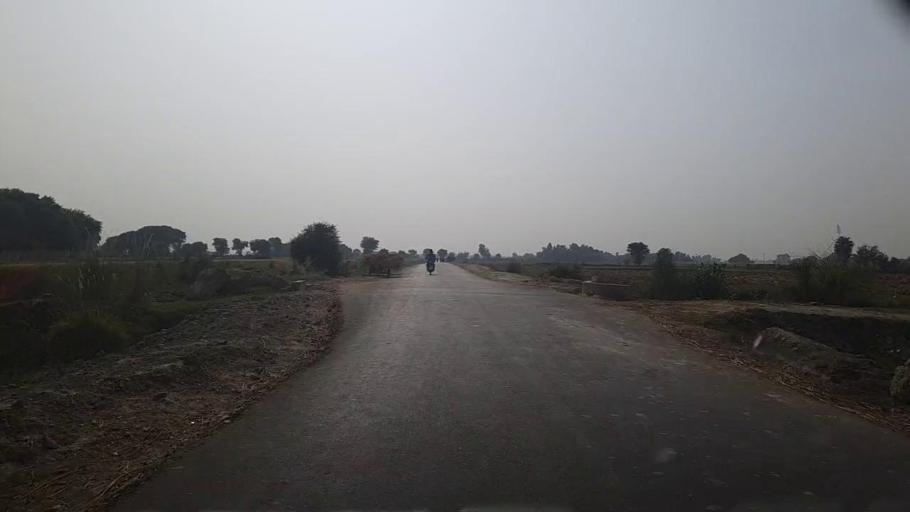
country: PK
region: Sindh
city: Kashmor
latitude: 28.4055
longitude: 69.5570
